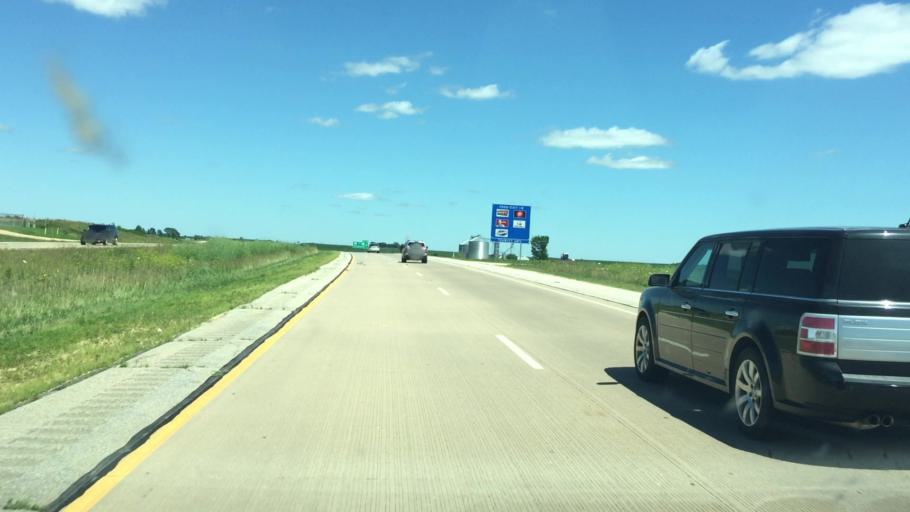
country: US
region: Wisconsin
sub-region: Grant County
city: Platteville
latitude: 42.7108
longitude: -90.4961
